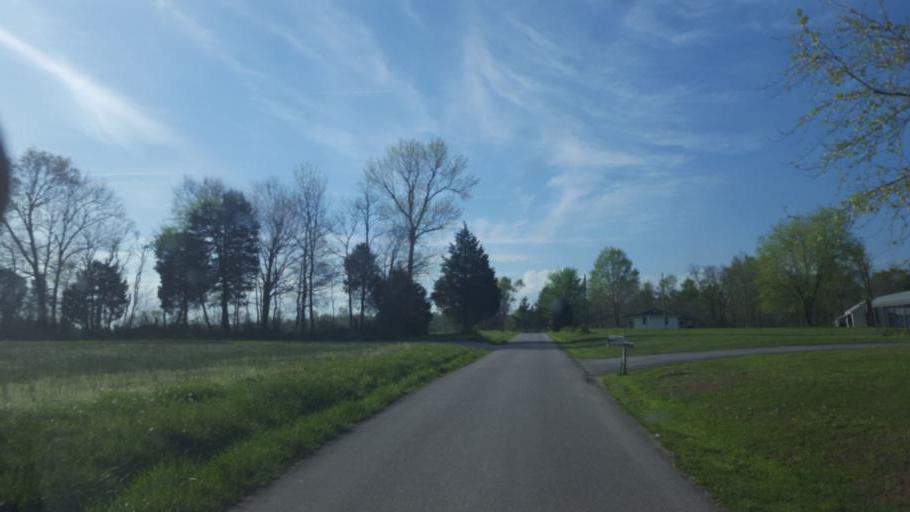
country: US
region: Kentucky
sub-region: Hart County
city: Munfordville
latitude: 37.3258
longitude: -86.0795
